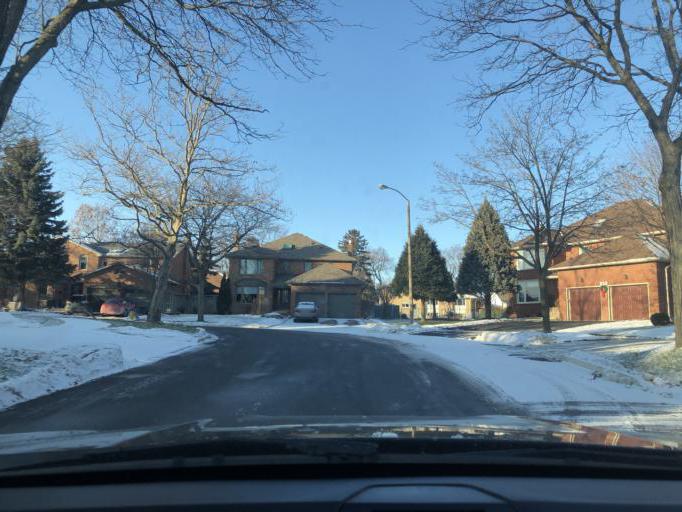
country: CA
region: Ontario
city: Scarborough
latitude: 43.7814
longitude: -79.1541
